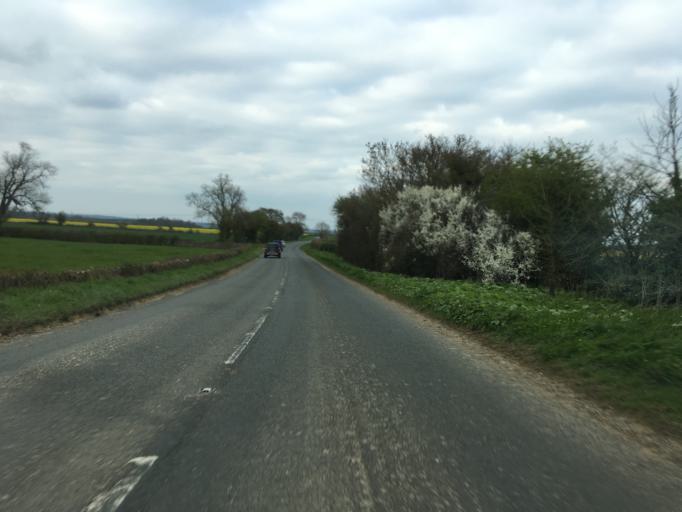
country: GB
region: England
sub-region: Gloucestershire
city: Northleach
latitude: 51.7670
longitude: -1.8198
